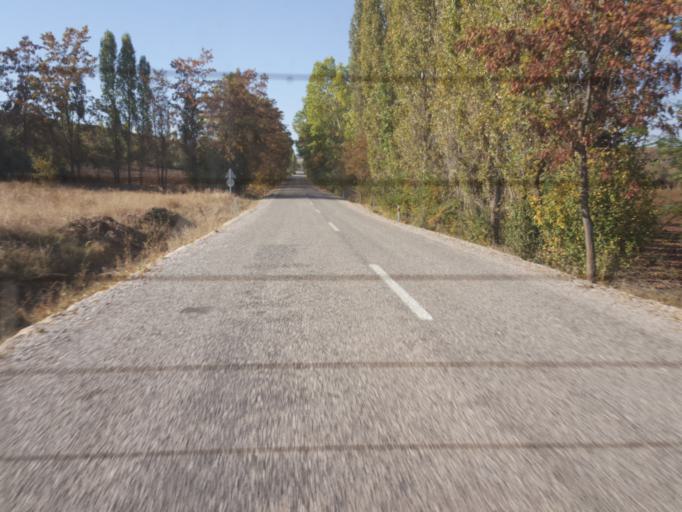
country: TR
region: Corum
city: Seydim
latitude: 40.5571
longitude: 34.7591
